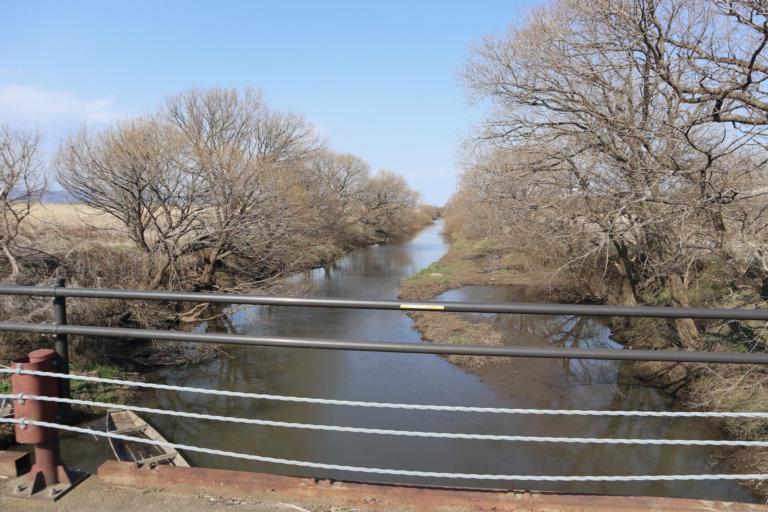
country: JP
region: Tochigi
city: Fujioka
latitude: 36.2605
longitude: 139.6854
